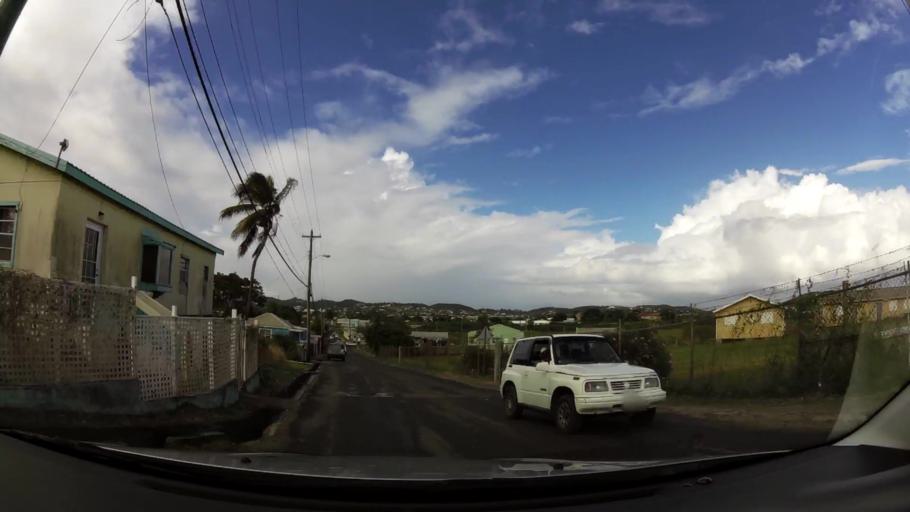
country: AG
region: Saint George
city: Piggotts
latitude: 17.1109
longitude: -61.8170
